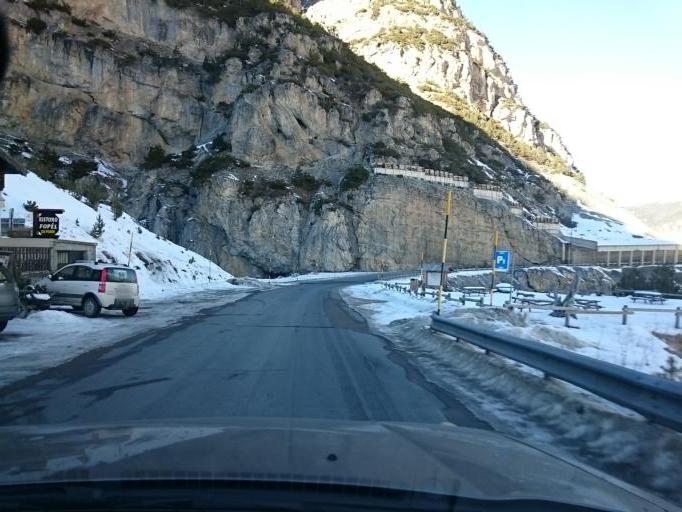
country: IT
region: Lombardy
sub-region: Provincia di Sondrio
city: Livigno
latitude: 46.6045
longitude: 10.1745
